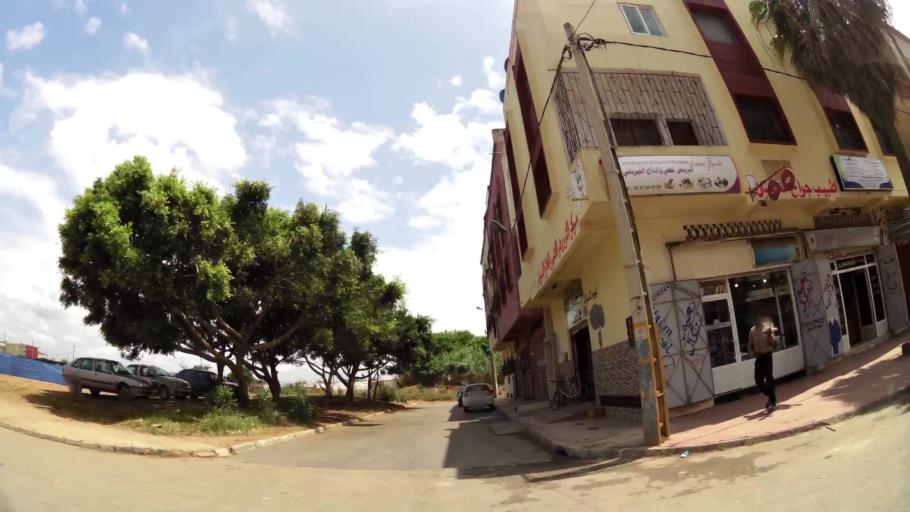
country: MA
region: Rabat-Sale-Zemmour-Zaer
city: Sale
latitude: 34.0466
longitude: -6.8196
